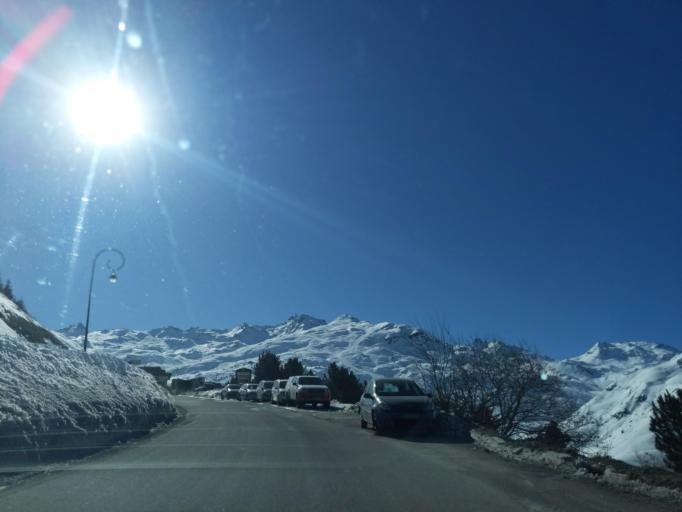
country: FR
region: Rhone-Alpes
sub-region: Departement de la Savoie
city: Val Thorens
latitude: 45.3179
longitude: 6.5412
